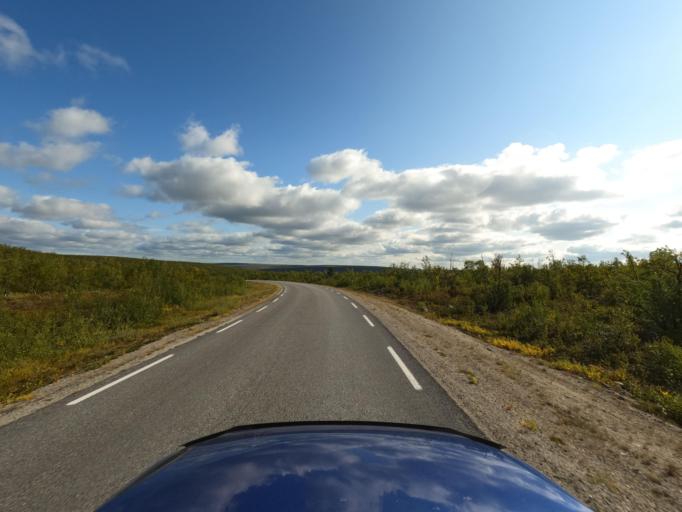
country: NO
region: Finnmark Fylke
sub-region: Porsanger
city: Lakselv
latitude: 69.3936
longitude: 24.5772
